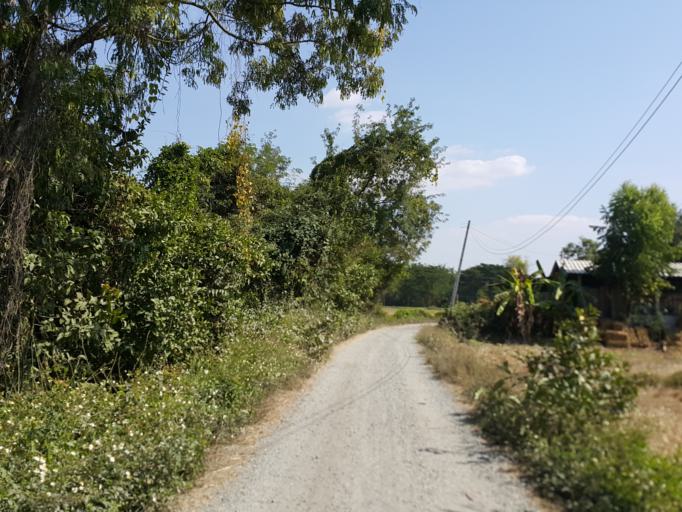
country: TH
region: Chiang Mai
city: San Kamphaeng
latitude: 18.7866
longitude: 99.1241
